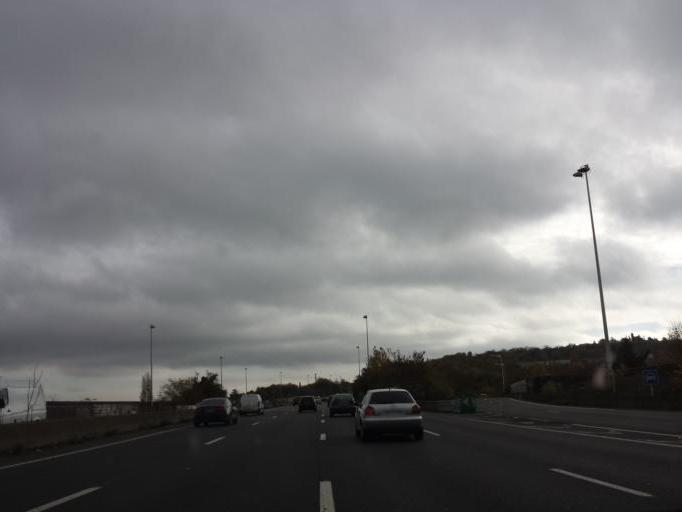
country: FR
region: Ile-de-France
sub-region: Departement du Val-d'Oise
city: Sannois
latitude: 48.9652
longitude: 2.2600
